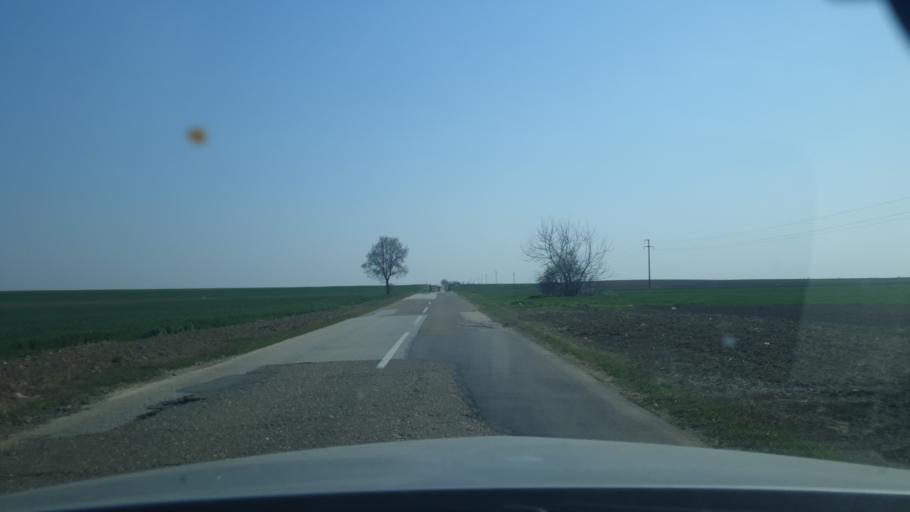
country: RS
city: Sasinci
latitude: 45.0396
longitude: 19.7344
